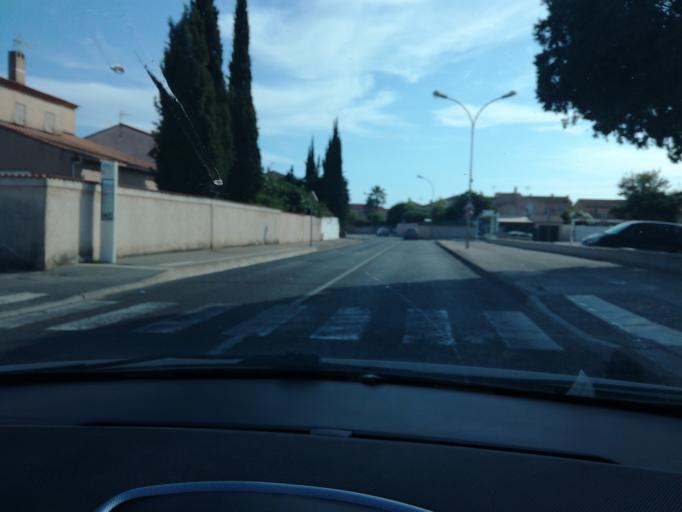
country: FR
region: Provence-Alpes-Cote d'Azur
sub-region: Departement du Var
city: La Crau
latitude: 43.1521
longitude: 6.0719
